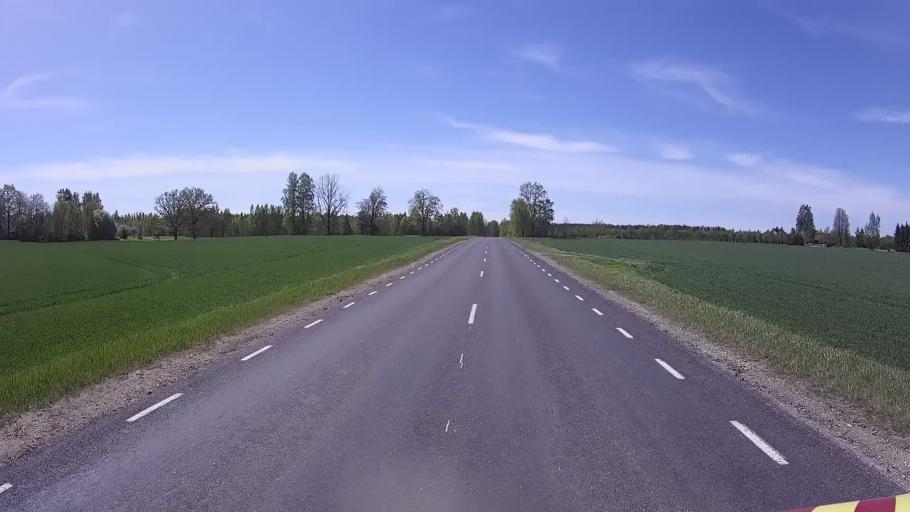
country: EE
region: Polvamaa
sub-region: Raepina vald
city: Rapina
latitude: 58.0171
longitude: 27.3651
